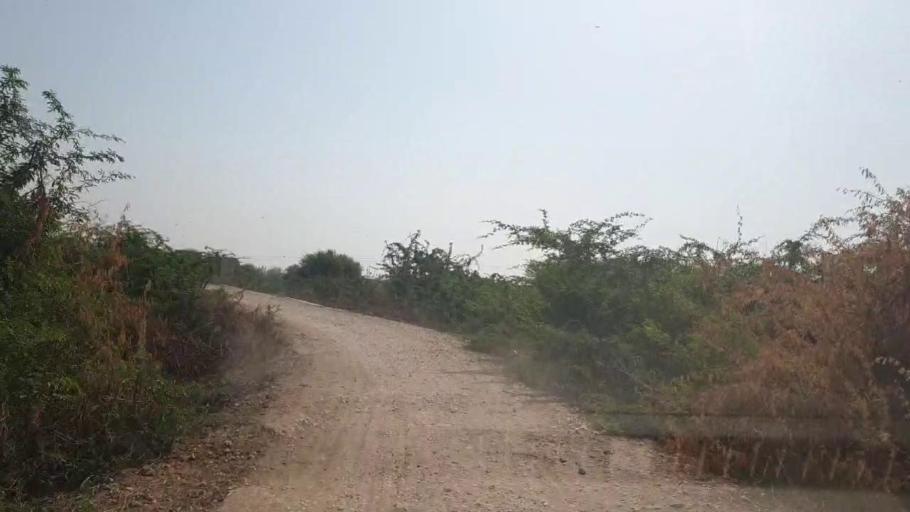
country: PK
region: Sindh
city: Berani
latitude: 25.8863
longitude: 68.7590
